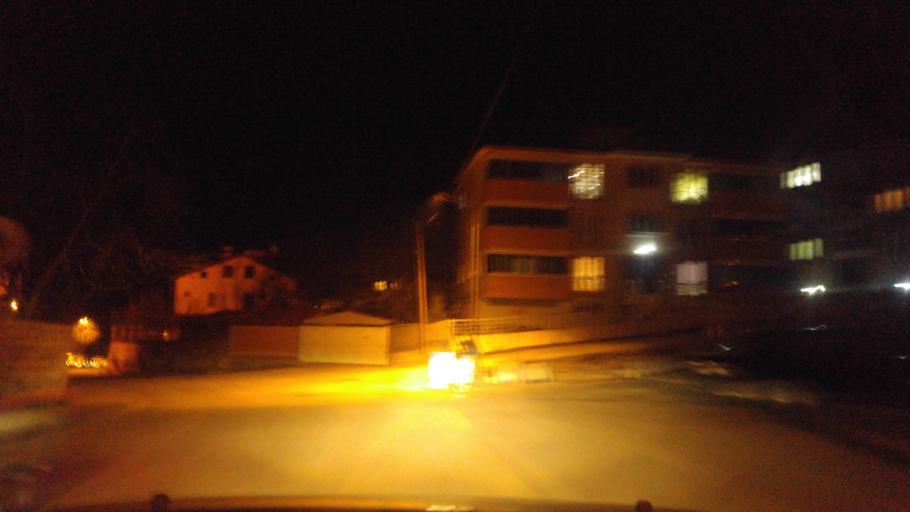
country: TR
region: Karabuk
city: Safranbolu
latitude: 41.2629
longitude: 32.6808
